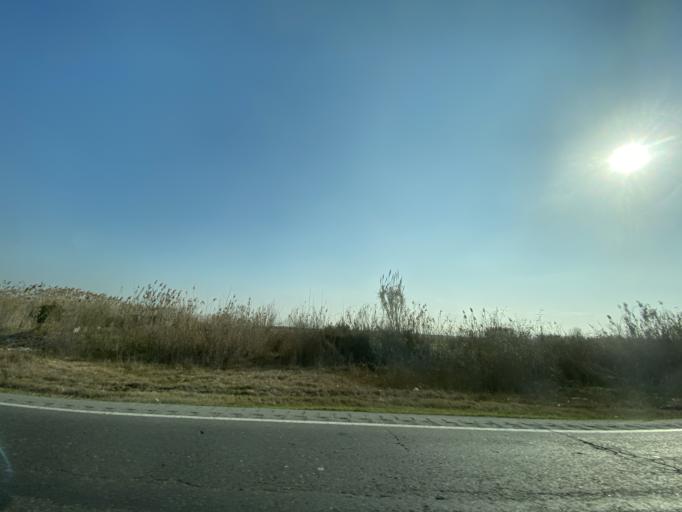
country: IR
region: Mazandaran
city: Babol
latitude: 36.5013
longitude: 52.5260
